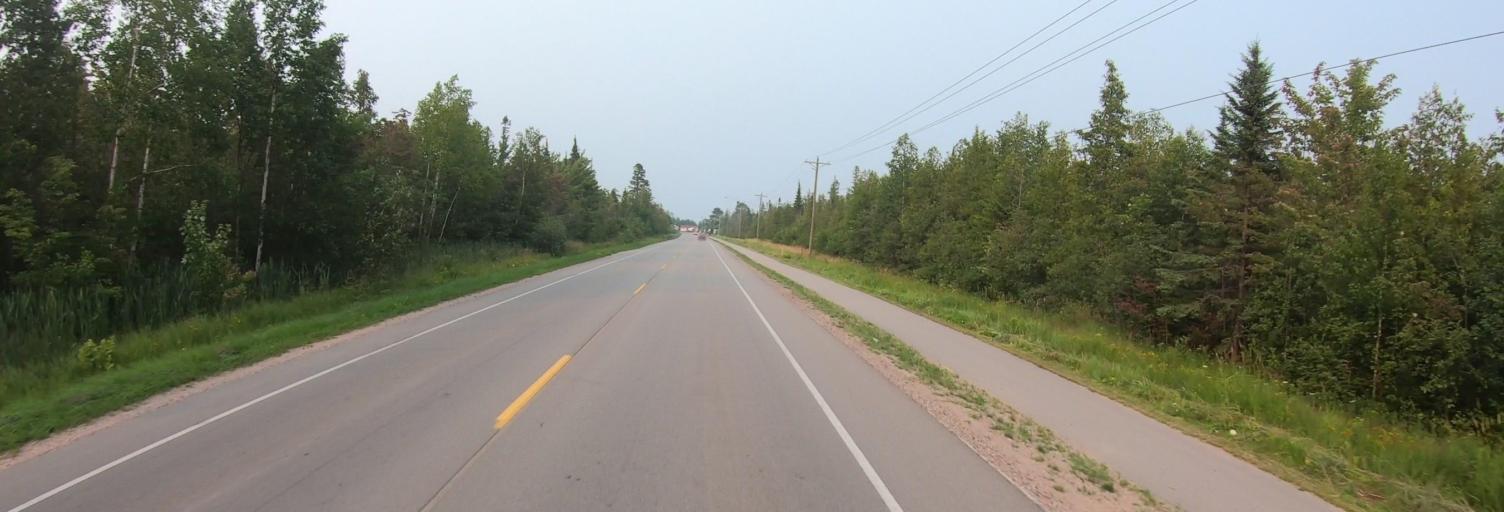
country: US
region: Michigan
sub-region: Chippewa County
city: Sault Ste. Marie
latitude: 46.4429
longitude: -84.6027
